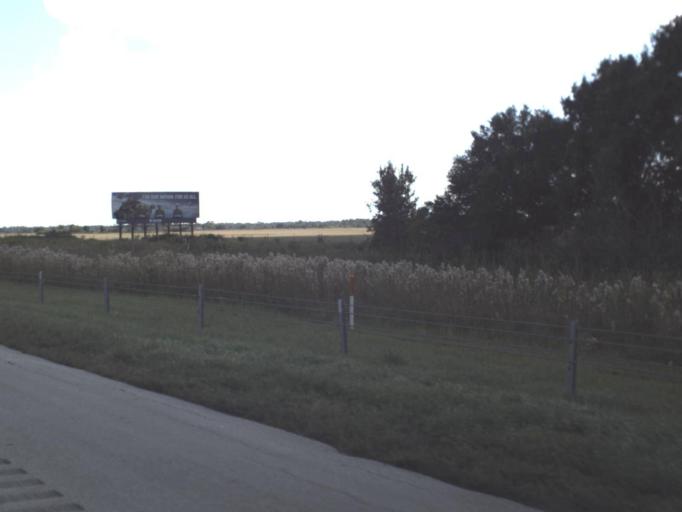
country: US
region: Florida
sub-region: Osceola County
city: Saint Cloud
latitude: 28.0482
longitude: -81.2163
